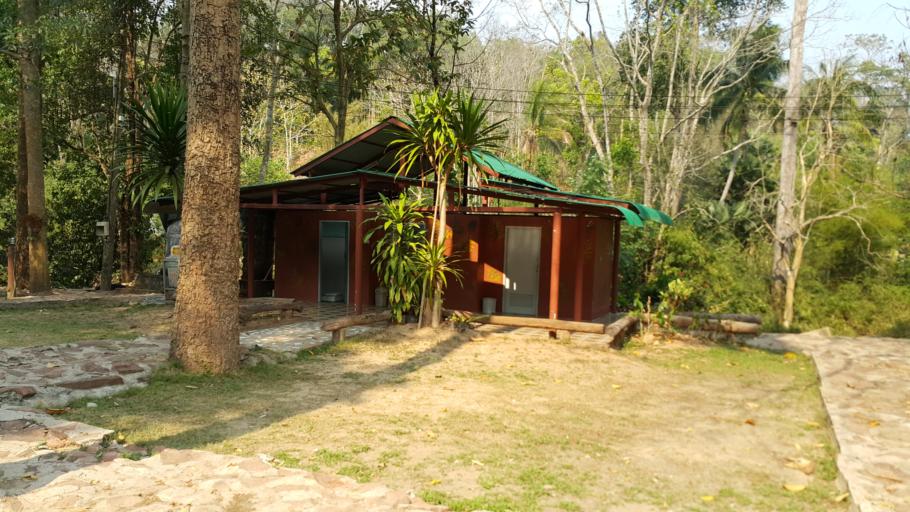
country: TH
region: Nakhon Phanom
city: Ban Phaeng
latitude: 17.9849
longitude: 104.1402
